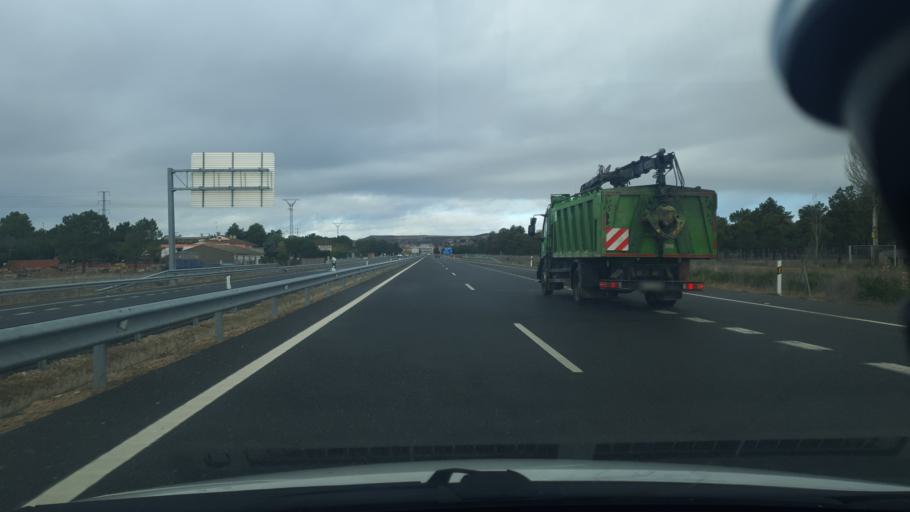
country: ES
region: Castille and Leon
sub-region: Provincia de Segovia
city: Cuellar
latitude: 41.3729
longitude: -4.3003
